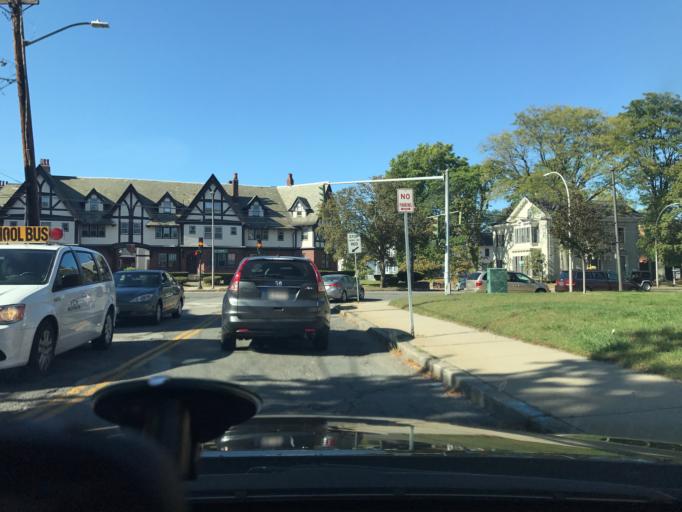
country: US
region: Massachusetts
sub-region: Middlesex County
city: Watertown
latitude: 42.3670
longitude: -71.1798
